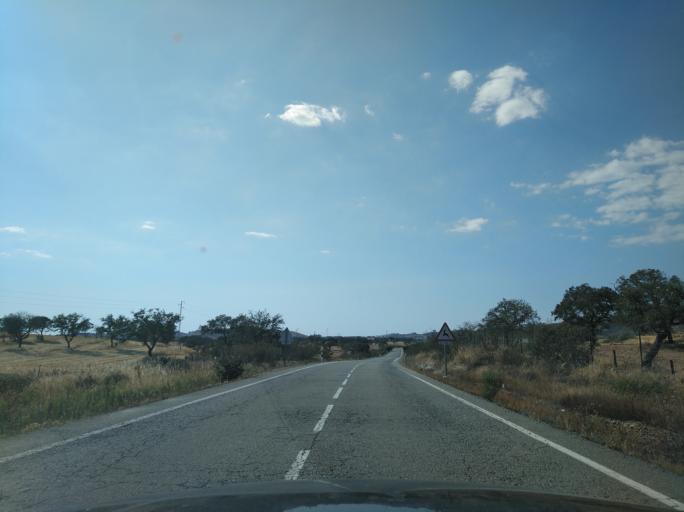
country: ES
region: Andalusia
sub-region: Provincia de Huelva
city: Santa Barbara de Casa
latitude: 37.7749
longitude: -7.1488
